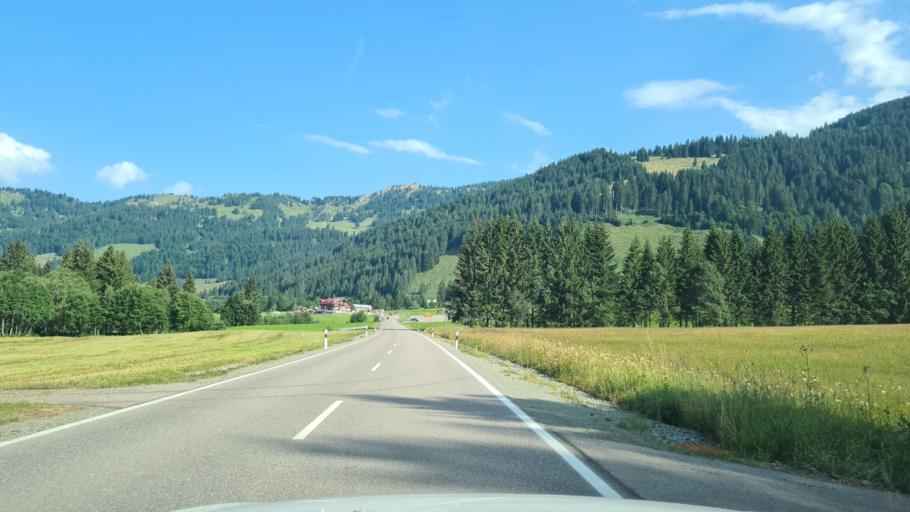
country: DE
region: Bavaria
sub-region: Swabia
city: Balderschwang
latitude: 47.4533
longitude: 10.1323
